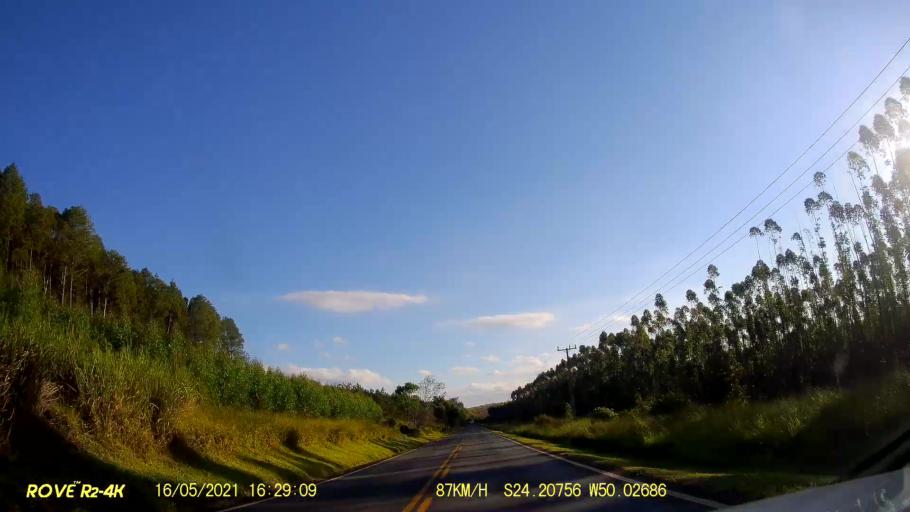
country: BR
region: Parana
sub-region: Jaguariaiva
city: Jaguariaiva
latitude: -24.2077
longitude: -50.0270
